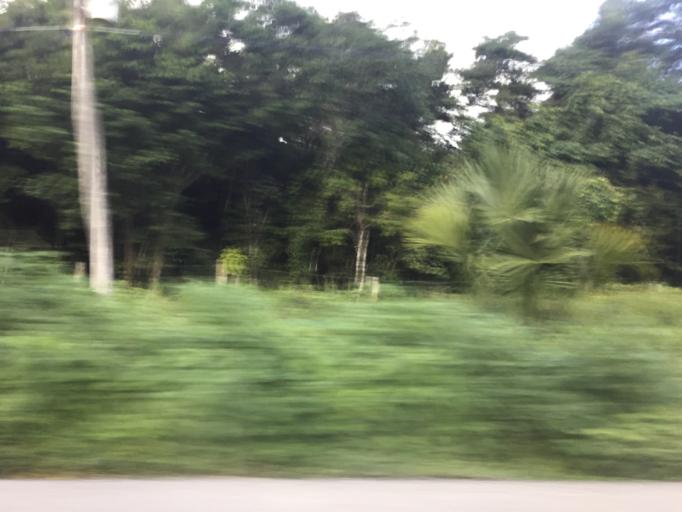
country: MX
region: Quintana Roo
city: Tulum
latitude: 20.2978
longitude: -87.5182
